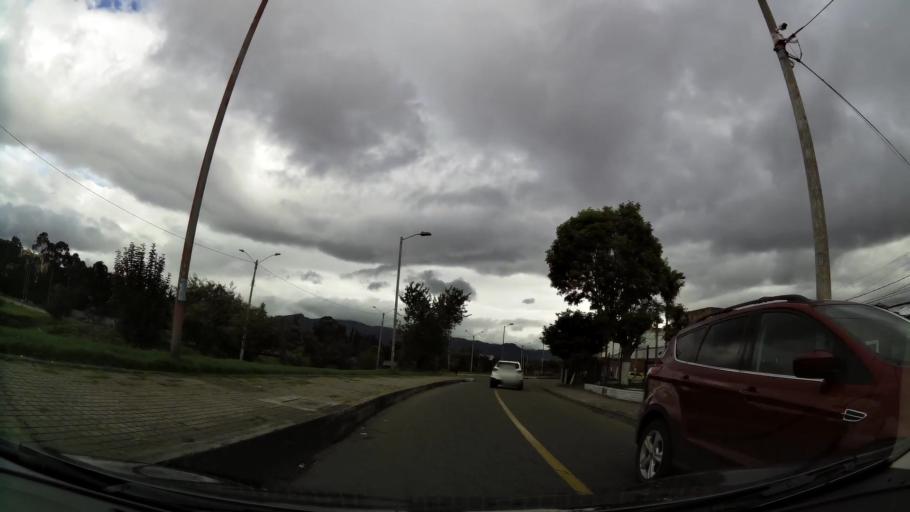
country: CO
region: Bogota D.C.
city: Barrio San Luis
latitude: 4.7133
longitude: -74.0946
